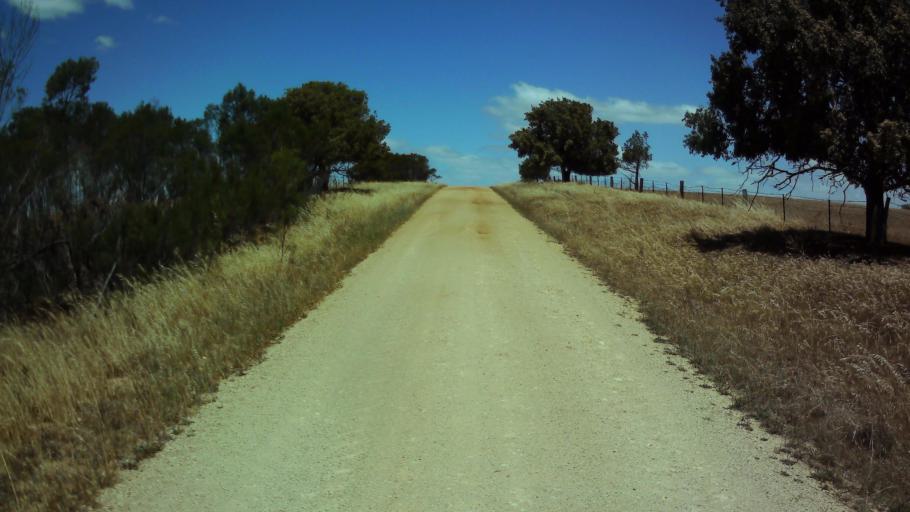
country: AU
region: New South Wales
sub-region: Weddin
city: Grenfell
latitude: -33.9566
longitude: 148.3654
